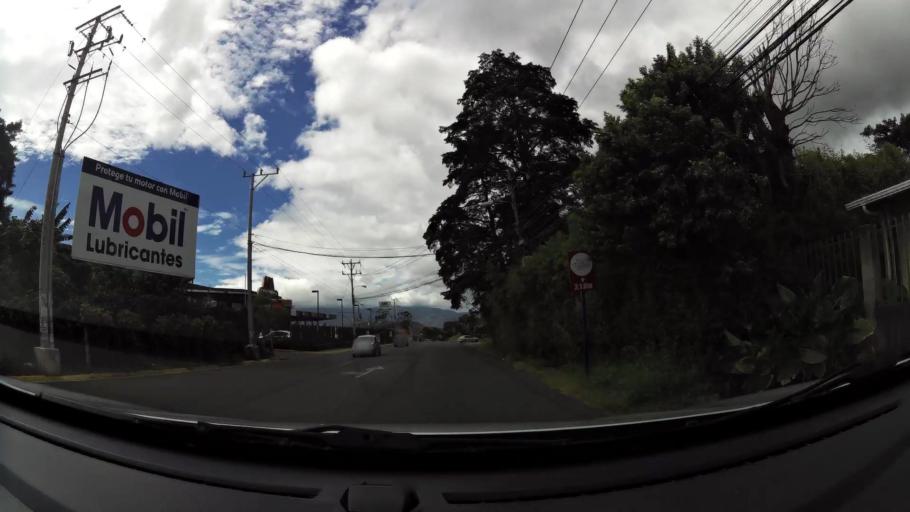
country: CR
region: Cartago
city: San Diego
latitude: 9.9095
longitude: -84.0024
